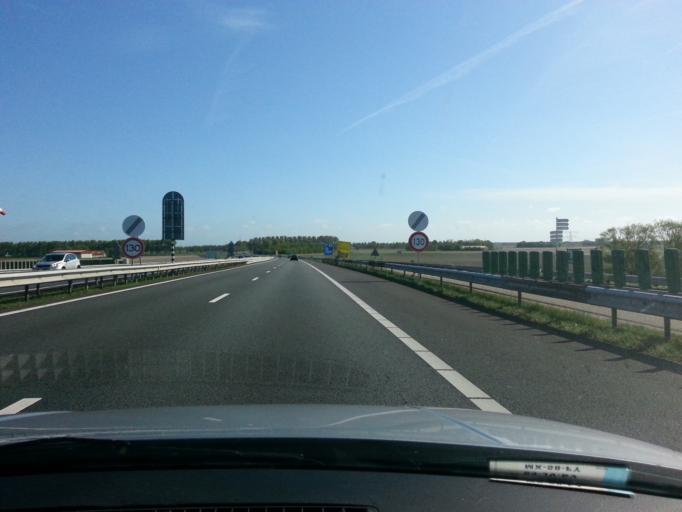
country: NL
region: Flevoland
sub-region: Gemeente Urk
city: Urk
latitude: 52.6154
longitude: 5.6510
